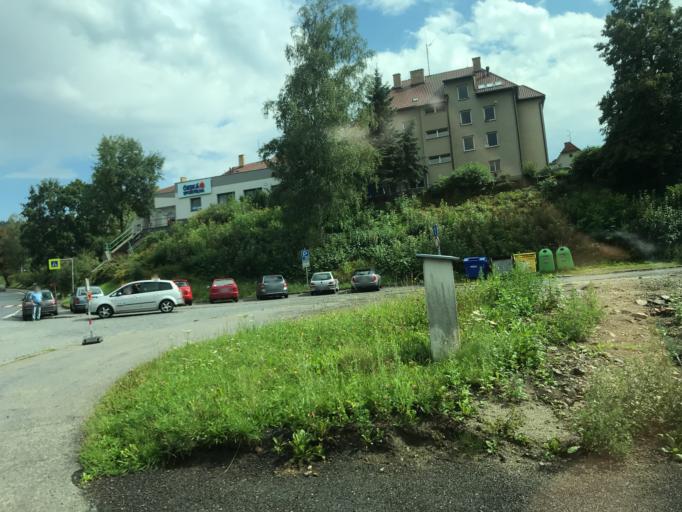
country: CZ
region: Jihocesky
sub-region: Okres Cesky Krumlov
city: Cesky Krumlov
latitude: 48.8115
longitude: 14.3236
